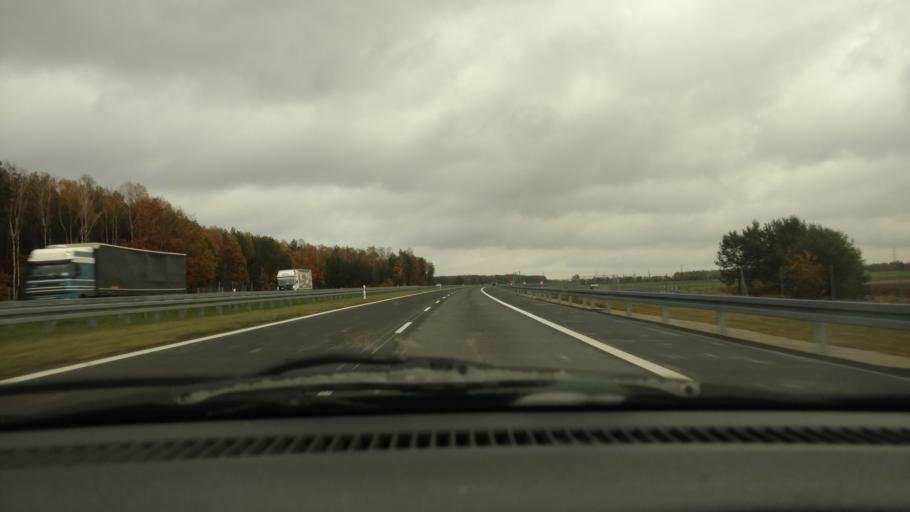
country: PL
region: Lodz Voivodeship
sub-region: Powiat pabianicki
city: Dobron
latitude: 51.6038
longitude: 19.2926
